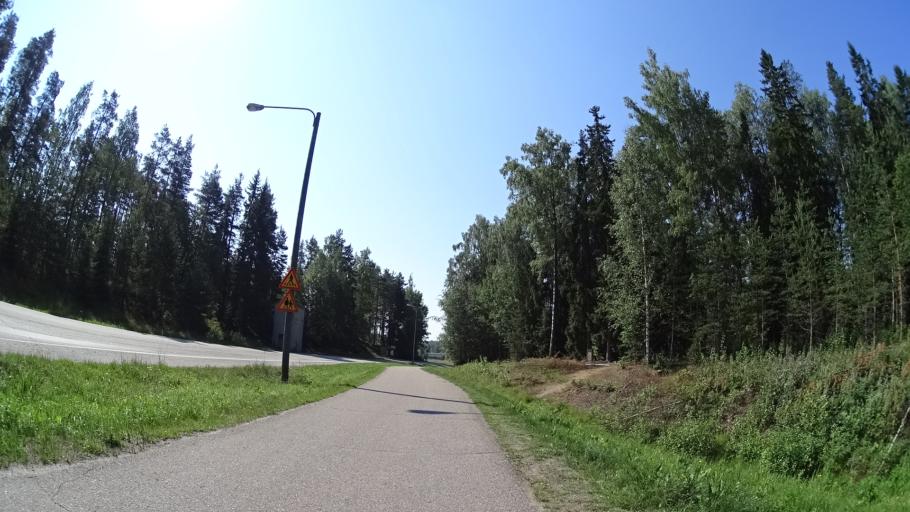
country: FI
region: Uusimaa
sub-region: Helsinki
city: Kerava
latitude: 60.3696
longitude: 25.0755
